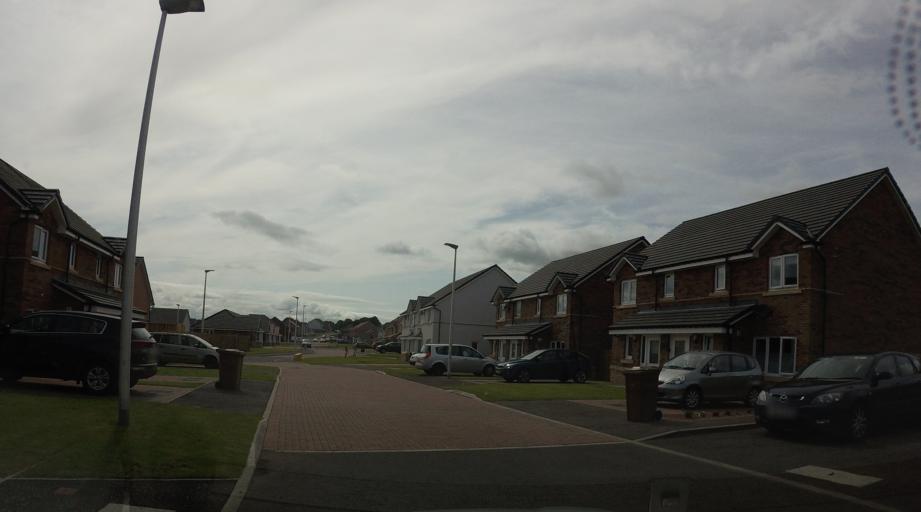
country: GB
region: Scotland
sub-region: West Lothian
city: Broxburn
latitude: 55.9383
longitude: -3.4956
